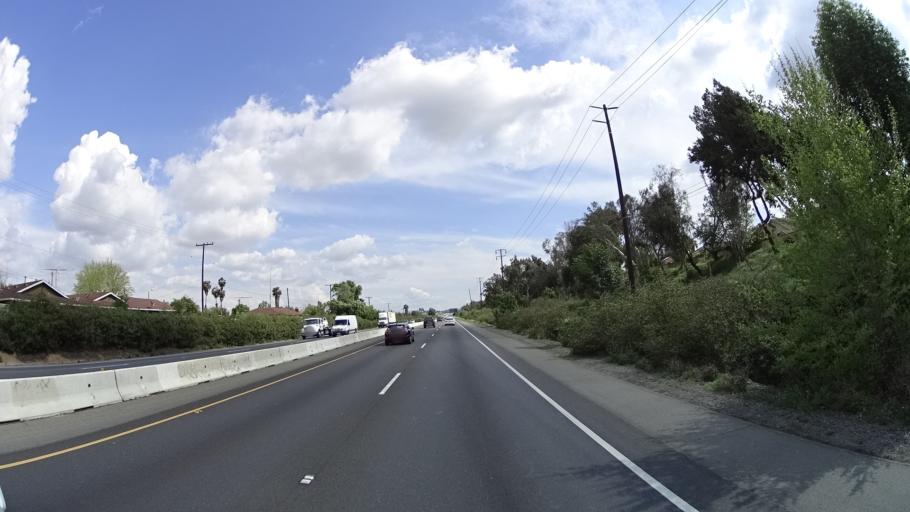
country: US
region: California
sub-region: Los Angeles County
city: Pomona
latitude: 34.0421
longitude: -117.7694
